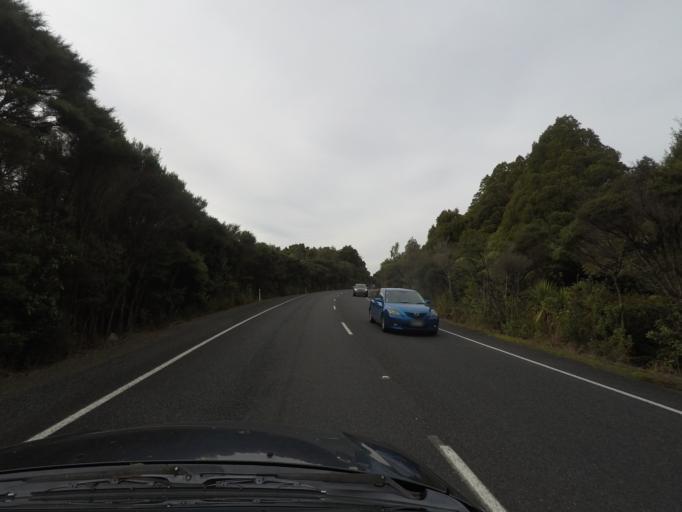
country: NZ
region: Auckland
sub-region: Auckland
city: Titirangi
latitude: -36.9439
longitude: 174.5313
